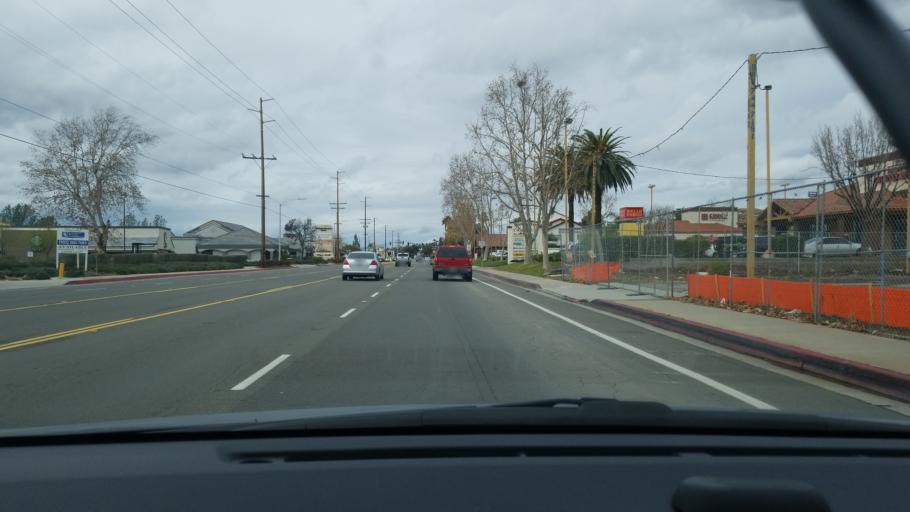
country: US
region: California
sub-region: Riverside County
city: Temecula
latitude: 33.5190
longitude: -117.1632
